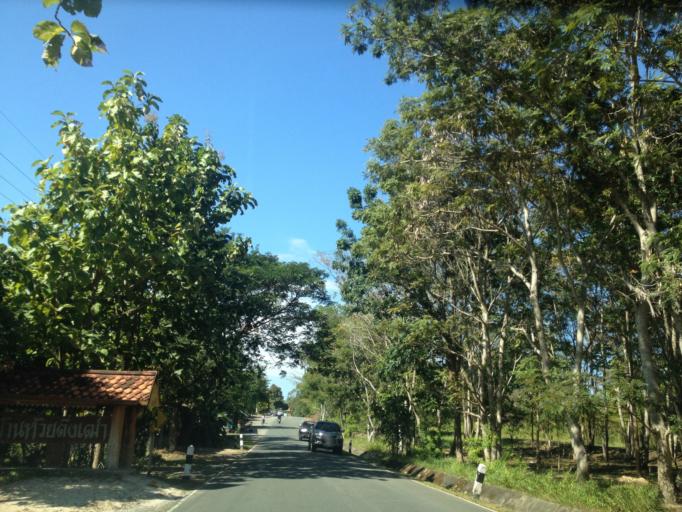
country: TH
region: Chiang Mai
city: Chiang Mai
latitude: 18.8624
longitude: 98.9482
